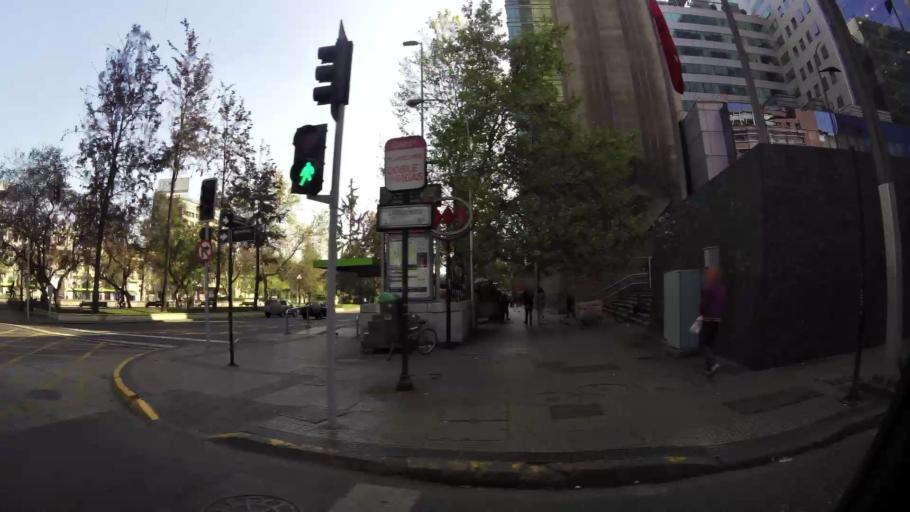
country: CL
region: Santiago Metropolitan
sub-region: Provincia de Santiago
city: Santiago
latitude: -33.4447
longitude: -70.6556
